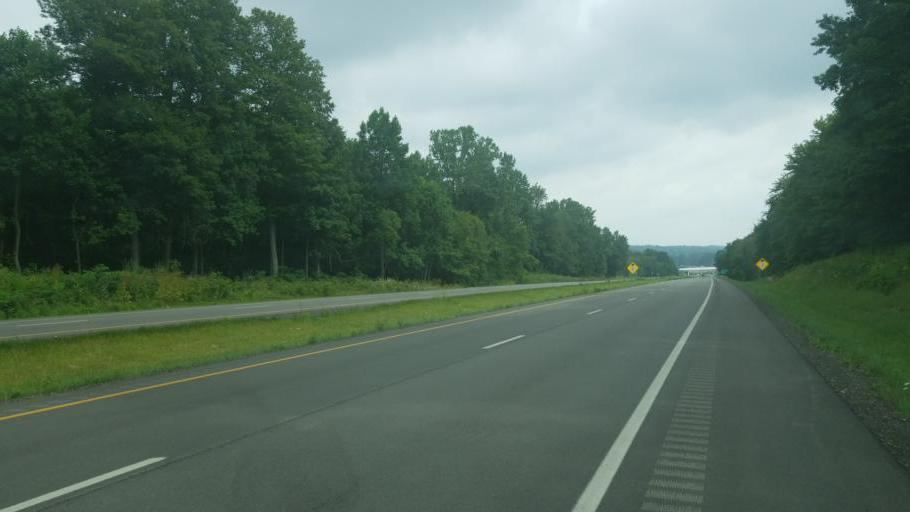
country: US
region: Ohio
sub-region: Sandusky County
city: Bellville
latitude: 40.6842
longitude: -82.5167
